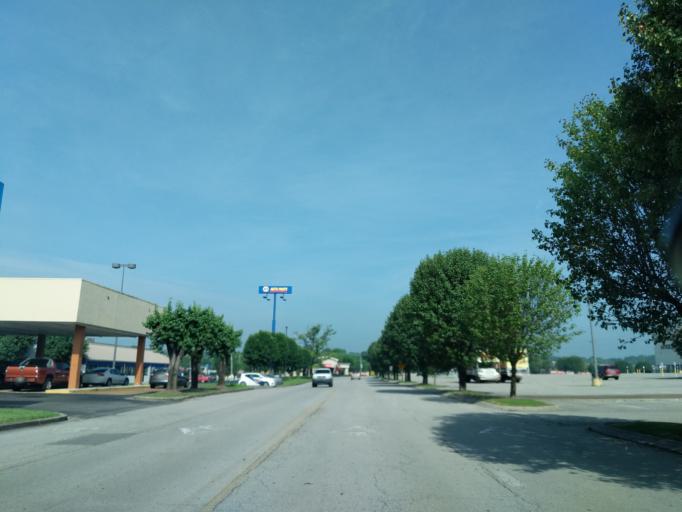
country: US
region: Tennessee
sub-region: Davidson County
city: Goodlettsville
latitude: 36.3008
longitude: -86.6985
